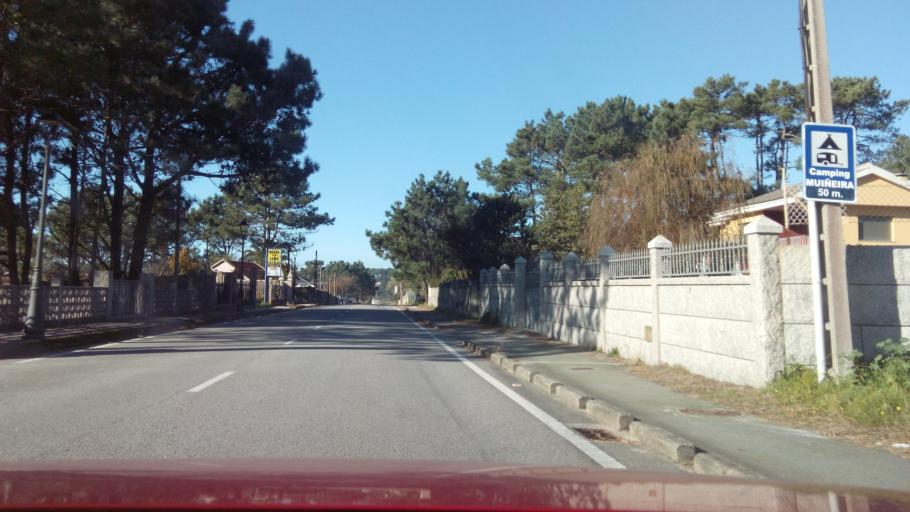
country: ES
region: Galicia
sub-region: Provincia de Pontevedra
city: O Grove
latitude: 42.4593
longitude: -8.8915
